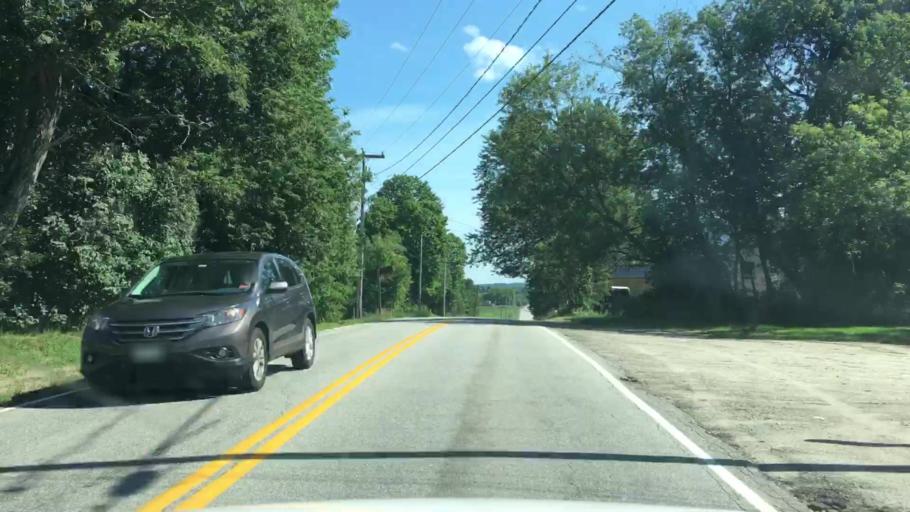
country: US
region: Maine
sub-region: Androscoggin County
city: Greene
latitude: 44.2195
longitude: -70.0917
